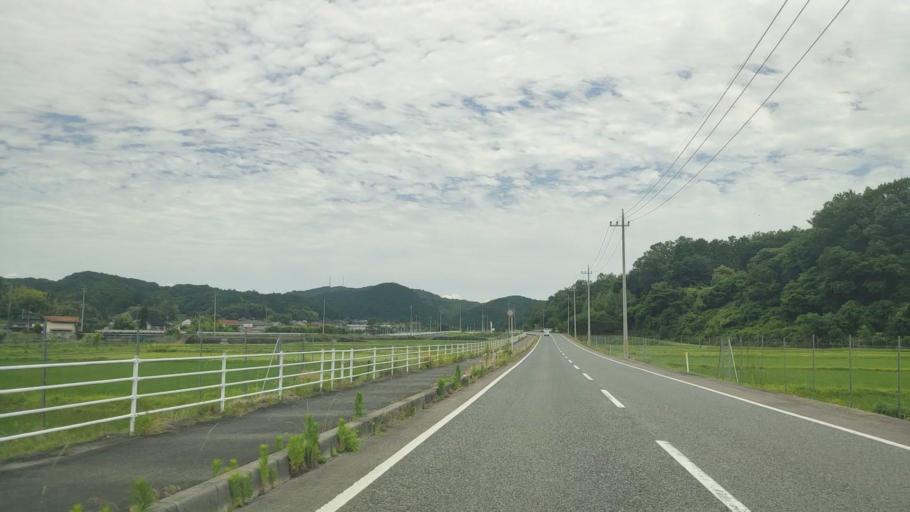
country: JP
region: Okayama
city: Tsuyama
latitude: 35.0653
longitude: 134.2012
